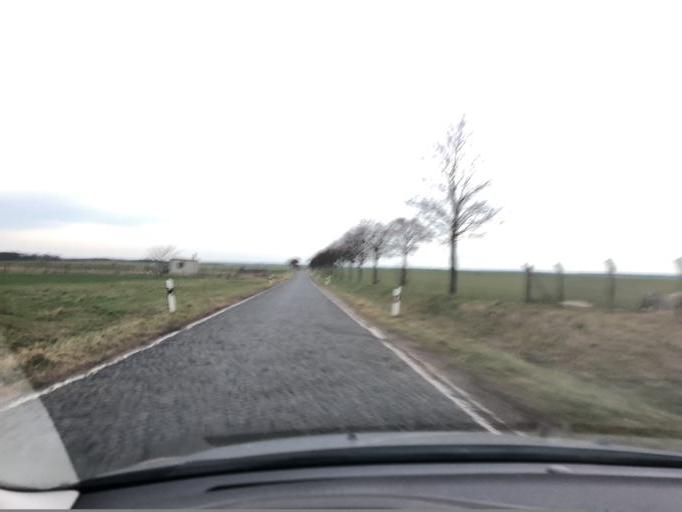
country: DE
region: Saxony-Anhalt
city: Laucha
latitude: 51.1790
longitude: 11.6440
